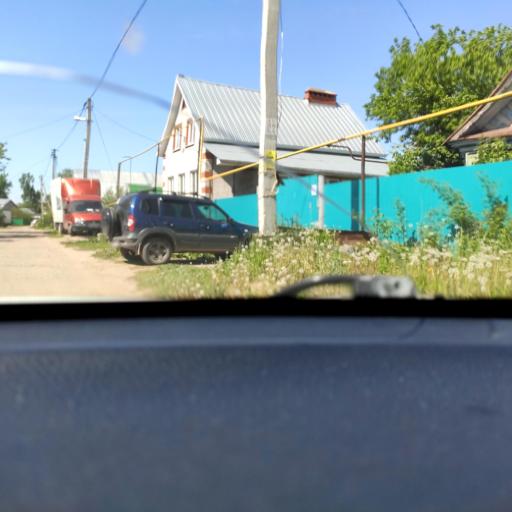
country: RU
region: Tatarstan
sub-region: Gorod Kazan'
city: Kazan
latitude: 55.8589
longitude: 49.1994
